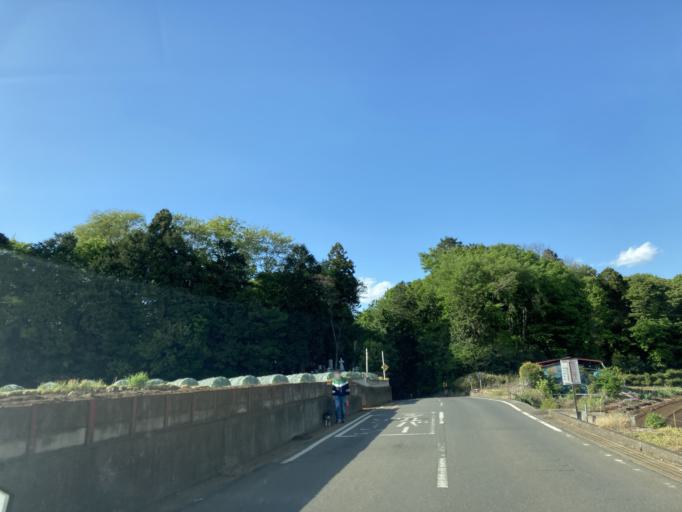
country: JP
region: Saitama
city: Sayama
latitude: 35.8636
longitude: 139.4401
